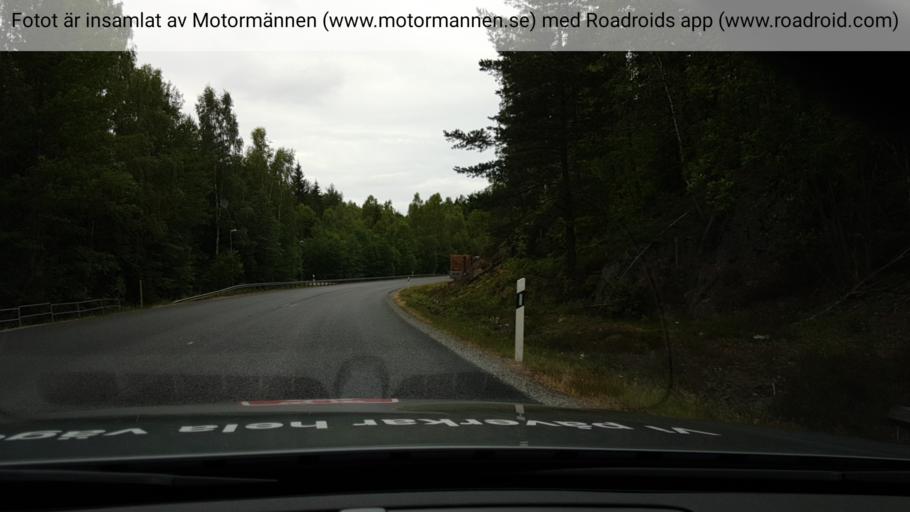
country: SE
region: Vaestmanland
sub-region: Skinnskattebergs Kommun
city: Skinnskatteberg
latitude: 59.8226
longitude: 15.5320
